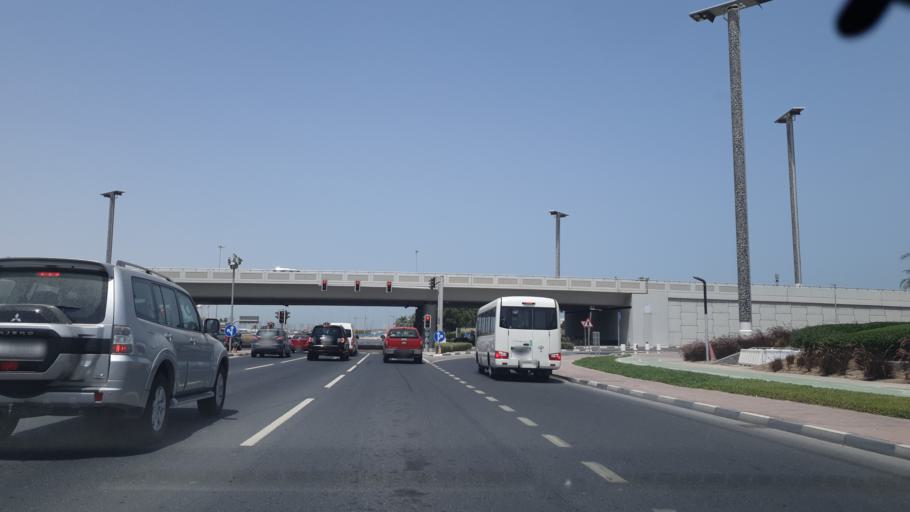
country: QA
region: Baladiyat ad Dawhah
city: Doha
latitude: 25.2829
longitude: 51.5519
